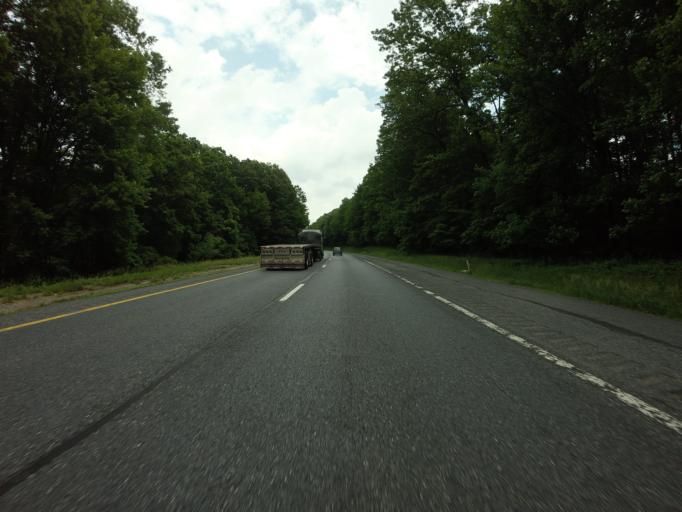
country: US
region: Maryland
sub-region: Frederick County
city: Jefferson
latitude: 39.3629
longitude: -77.5089
